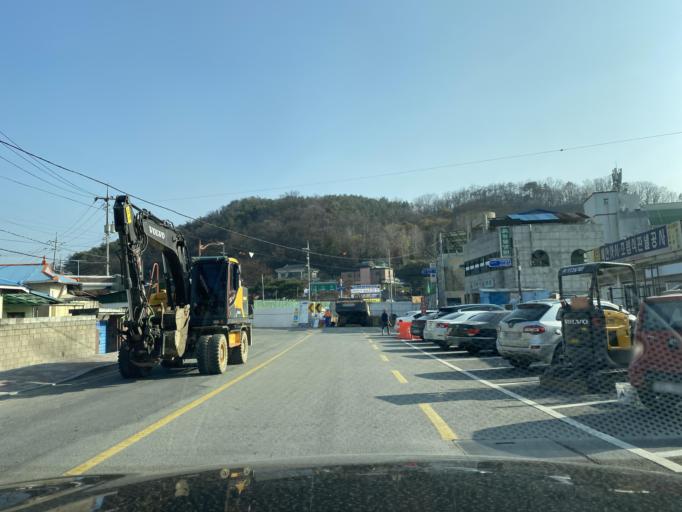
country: KR
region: Chungcheongnam-do
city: Yesan
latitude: 36.6814
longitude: 126.8519
